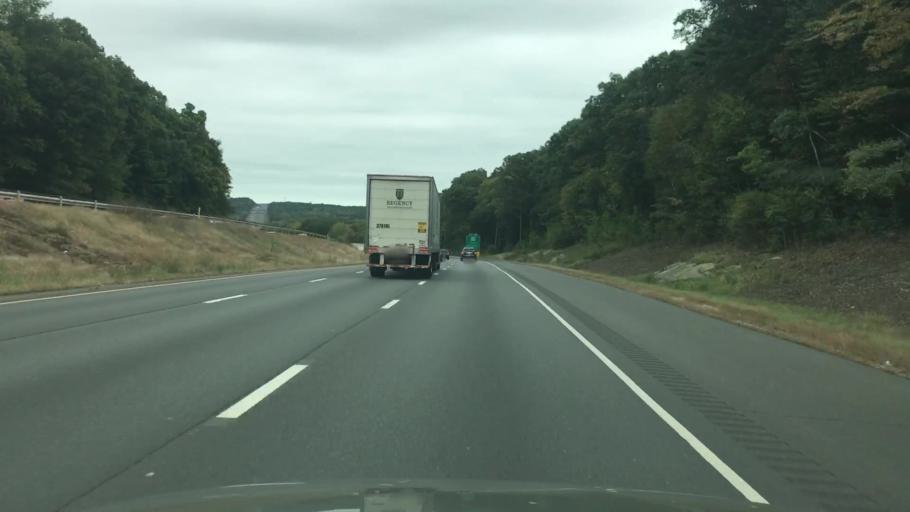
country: US
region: Connecticut
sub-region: Tolland County
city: Tolland
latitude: 41.8563
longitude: -72.3763
